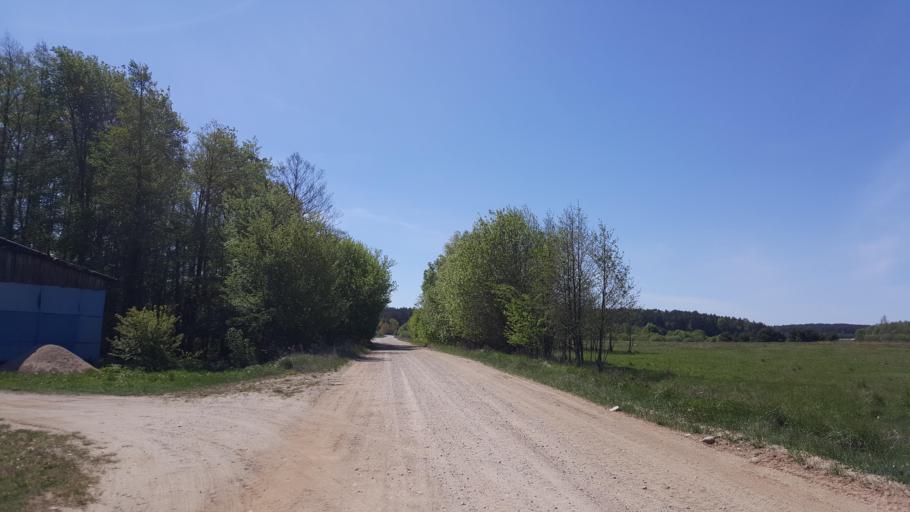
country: BY
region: Brest
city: Zhabinka
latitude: 52.3912
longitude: 24.0031
